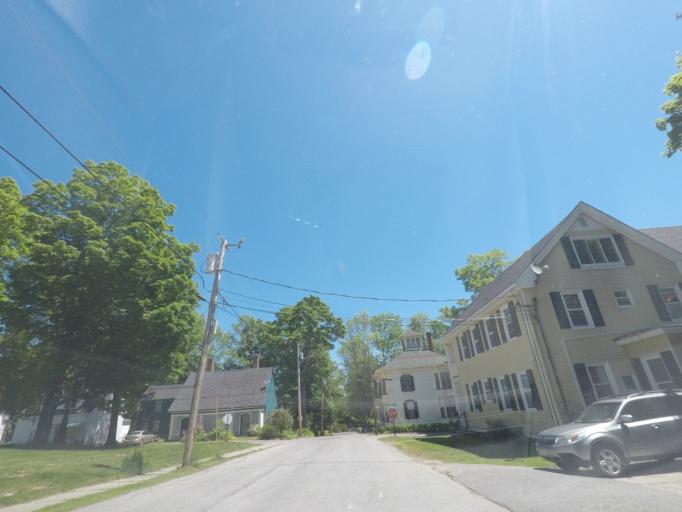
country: US
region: Maine
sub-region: Kennebec County
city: Gardiner
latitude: 44.2268
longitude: -69.7733
